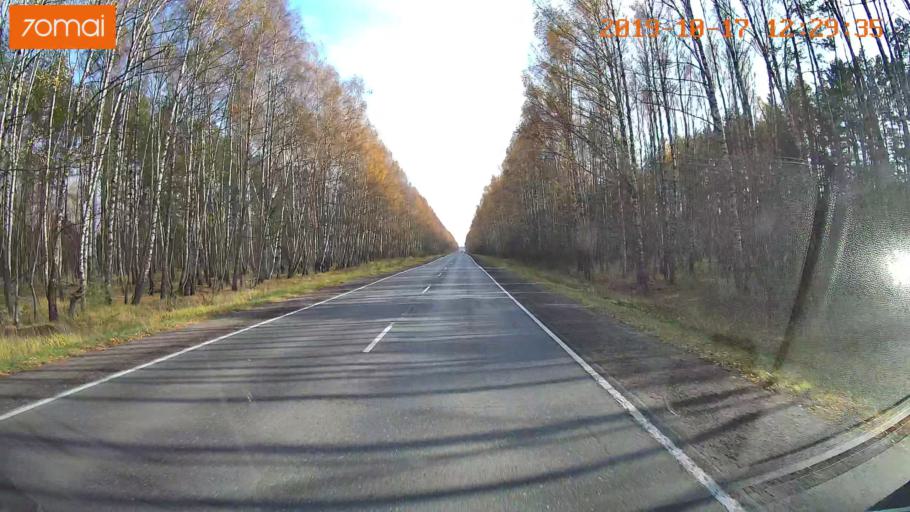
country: RU
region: Rjazan
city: Syntul
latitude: 54.9806
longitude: 41.2957
